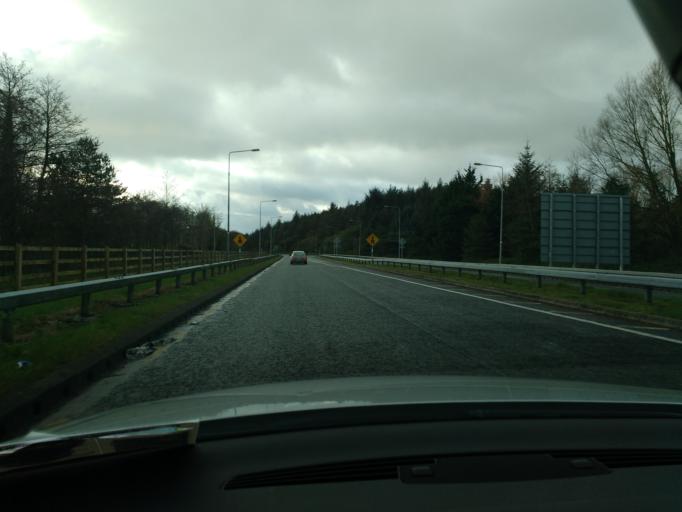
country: IE
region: Munster
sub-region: An Clar
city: Shannon
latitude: 52.7022
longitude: -8.8957
